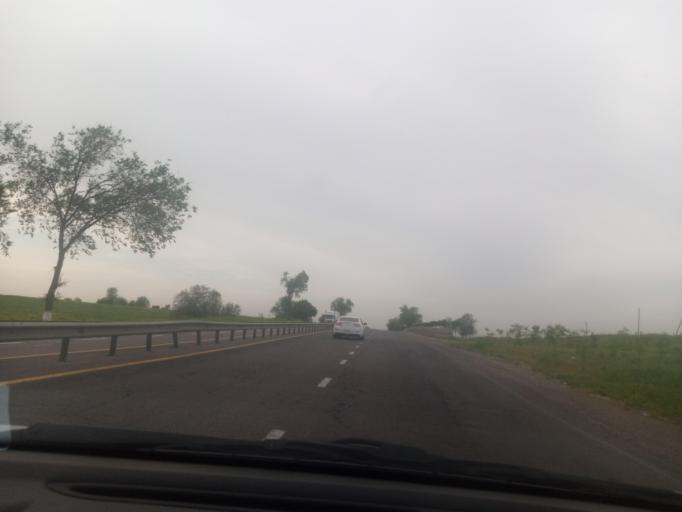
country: UZ
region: Toshkent
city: Tuytepa
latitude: 41.1103
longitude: 69.4490
